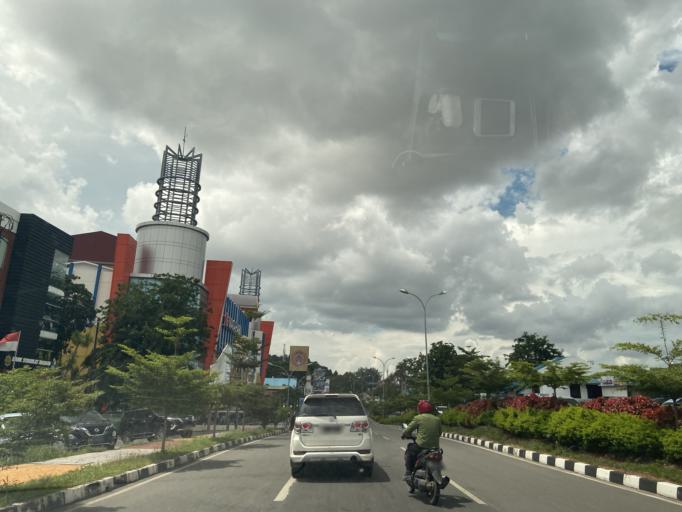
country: SG
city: Singapore
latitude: 1.1314
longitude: 104.0095
